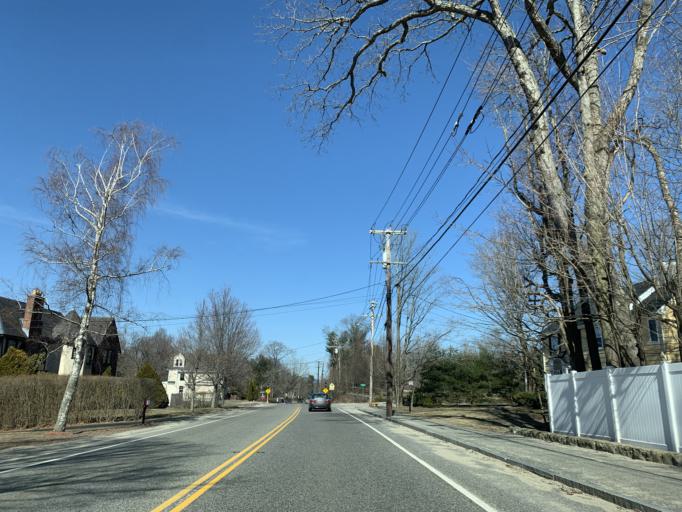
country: US
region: Massachusetts
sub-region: Norfolk County
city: Sharon
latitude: 42.1309
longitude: -71.1739
